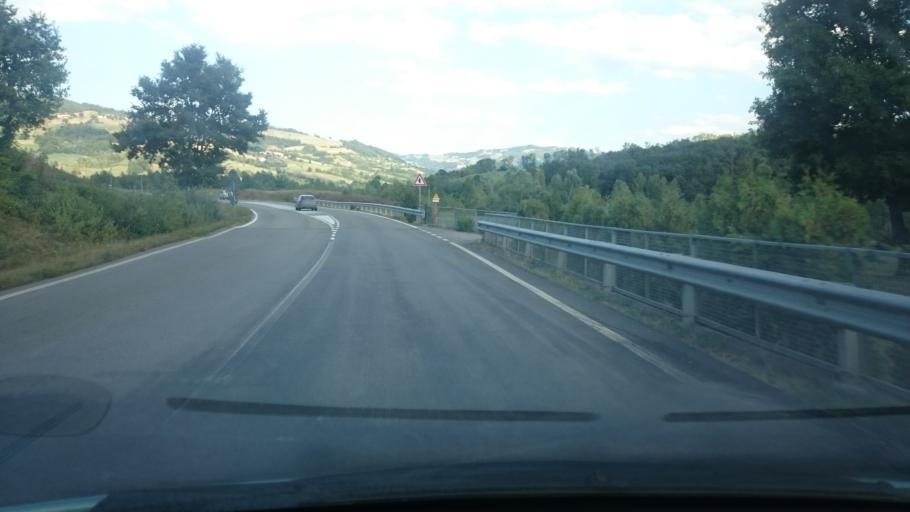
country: IT
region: Emilia-Romagna
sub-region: Provincia di Reggio Emilia
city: Toano
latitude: 44.4187
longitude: 10.5600
